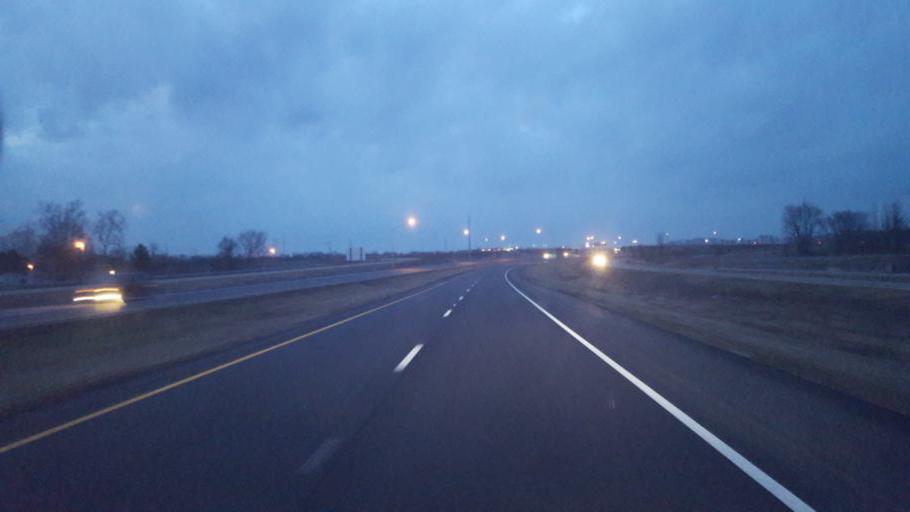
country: US
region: Ohio
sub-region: Ross County
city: Chillicothe
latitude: 39.4093
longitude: -82.9754
